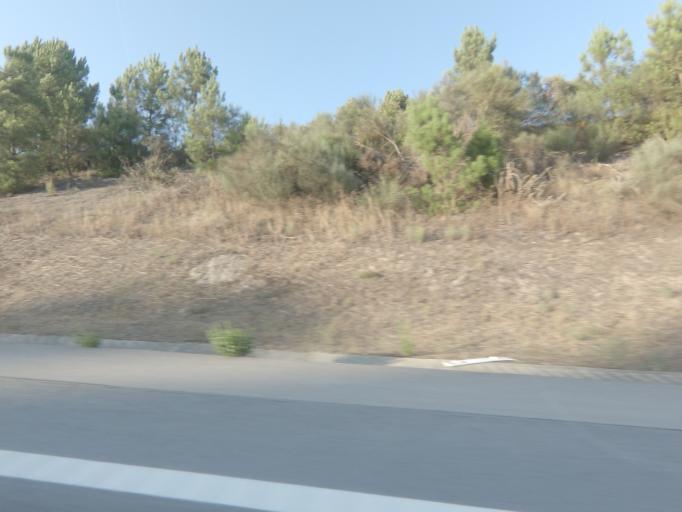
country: PT
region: Vila Real
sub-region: Vila Real
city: Vila Real
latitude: 41.3124
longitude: -7.6882
